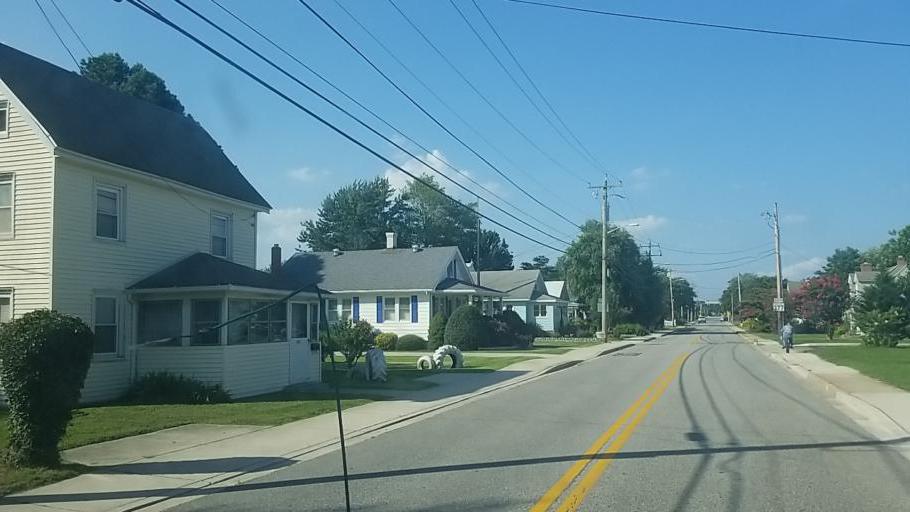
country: US
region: Maryland
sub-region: Worcester County
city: Berlin
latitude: 38.3286
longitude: -75.2162
